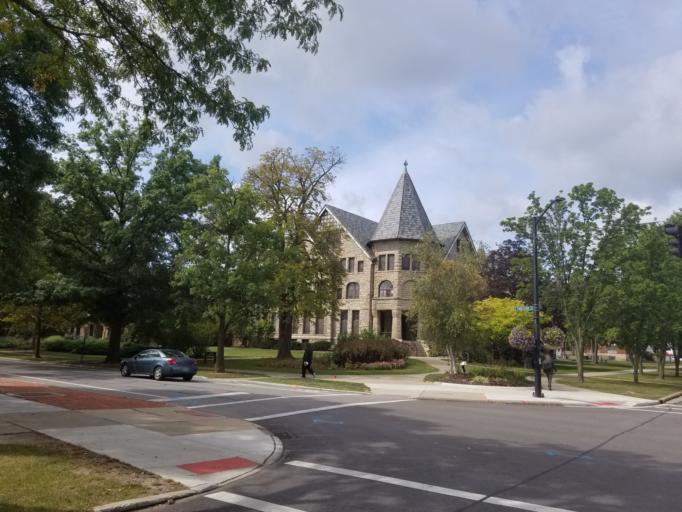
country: US
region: Ohio
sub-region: Lorain County
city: Oberlin
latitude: 41.2917
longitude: -82.2199
